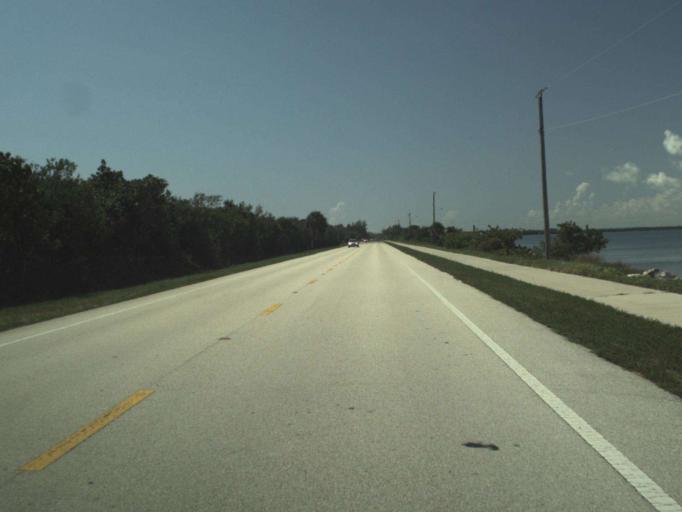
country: US
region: Florida
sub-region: Indian River County
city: Sebastian
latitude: 27.8379
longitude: -80.4369
